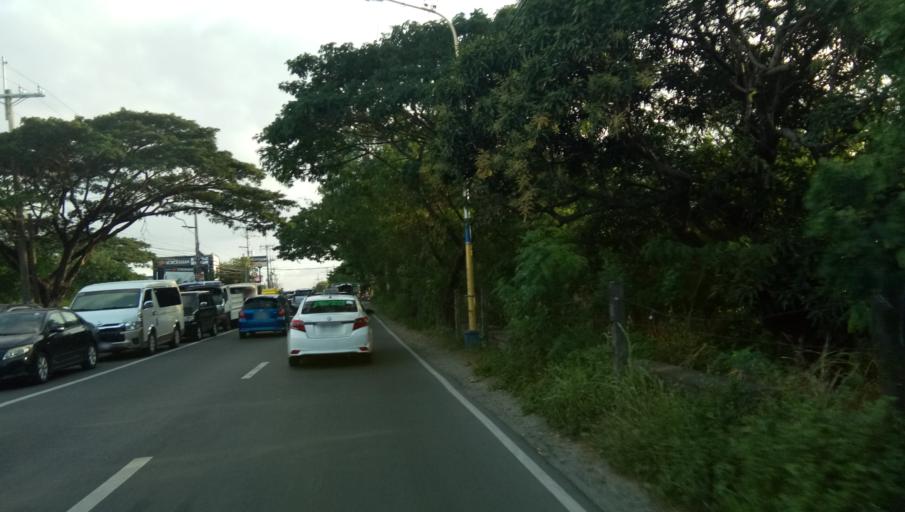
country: PH
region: Calabarzon
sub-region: Province of Cavite
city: Dasmarinas
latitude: 14.3775
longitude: 120.9792
